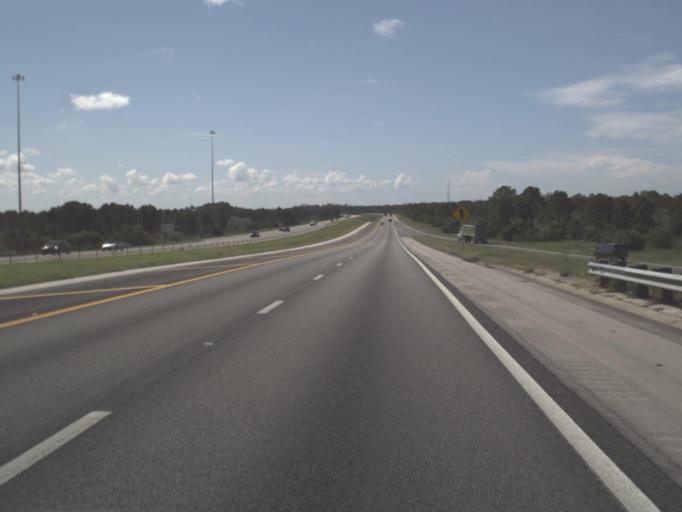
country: US
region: Florida
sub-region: Charlotte County
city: Charlotte Park
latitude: 26.8565
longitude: -81.9710
